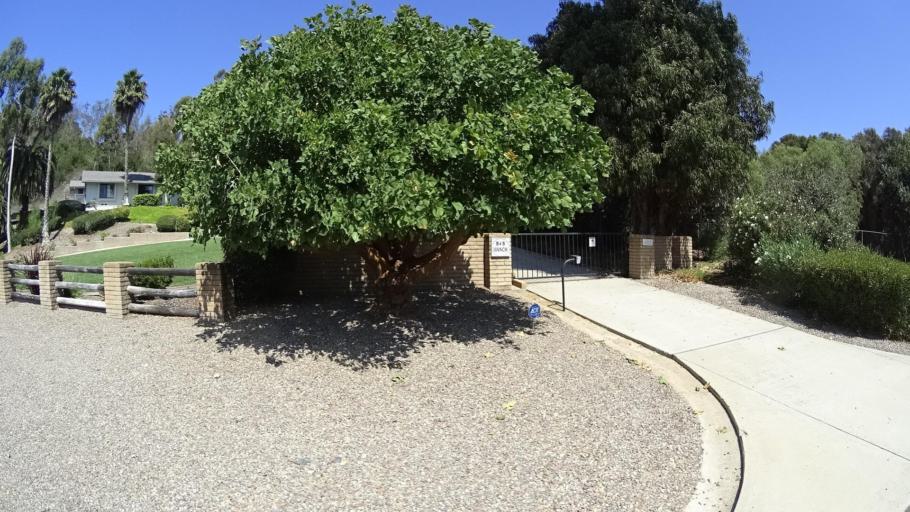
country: US
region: California
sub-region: San Diego County
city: Fairbanks Ranch
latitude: 32.9955
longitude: -117.2137
